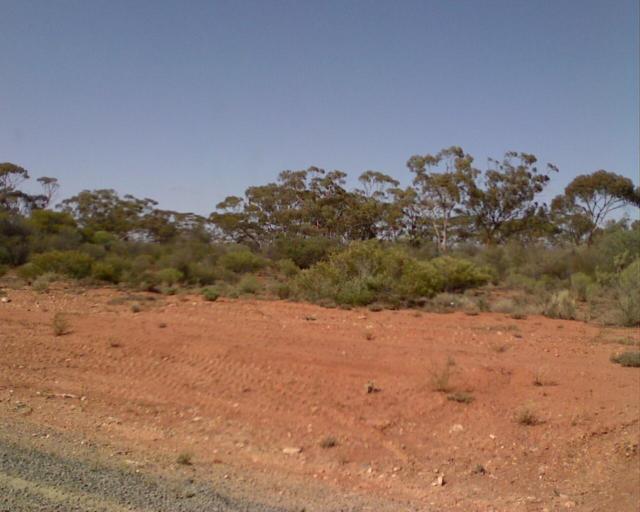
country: AU
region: Western Australia
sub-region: Kalgoorlie/Boulder
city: Boulder
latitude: -30.8387
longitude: 121.3862
